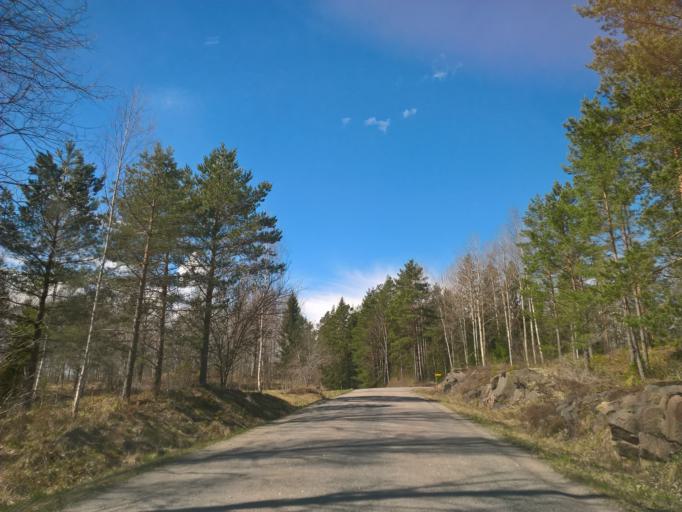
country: SE
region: OEstergoetland
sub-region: Finspangs Kommun
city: Finspang
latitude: 58.7293
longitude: 15.7392
